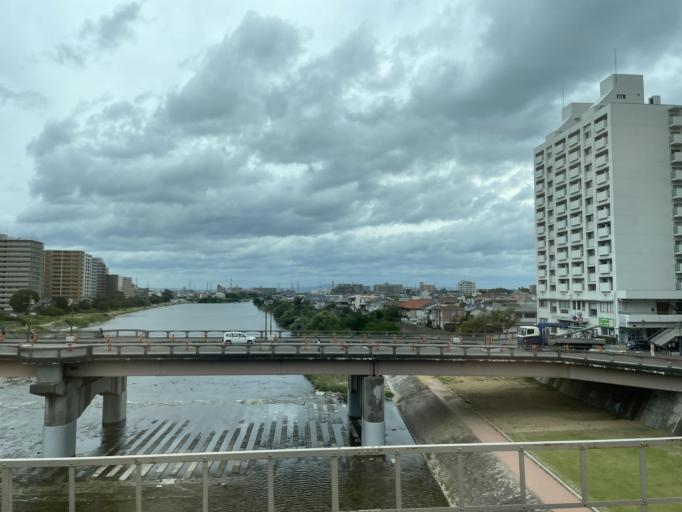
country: JP
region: Hyogo
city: Takarazuka
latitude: 34.8055
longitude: 135.3464
